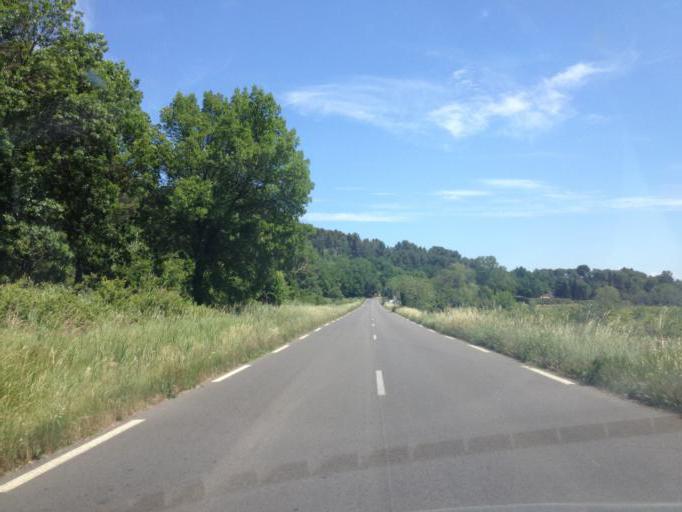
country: FR
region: Provence-Alpes-Cote d'Azur
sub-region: Departement du Vaucluse
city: Cadenet
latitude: 43.7411
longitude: 5.3456
